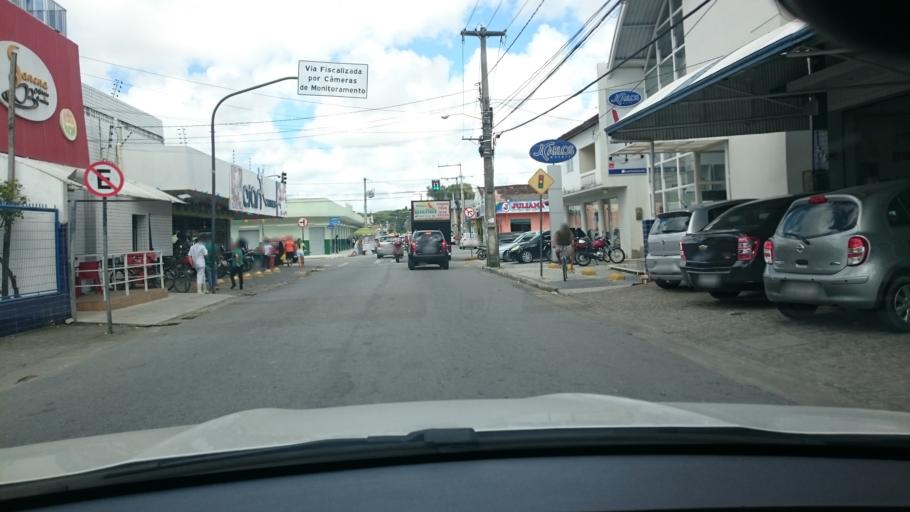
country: BR
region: Paraiba
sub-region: Joao Pessoa
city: Joao Pessoa
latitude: -7.1247
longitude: -34.8637
